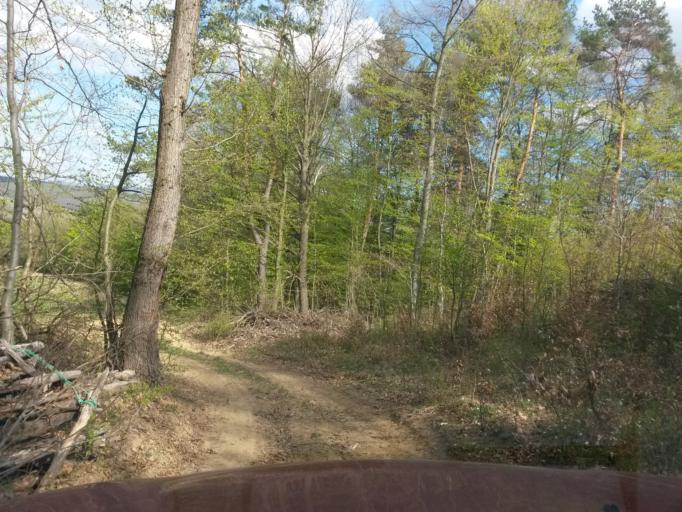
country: SK
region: Presovsky
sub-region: Okres Presov
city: Presov
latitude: 48.9561
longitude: 21.1320
